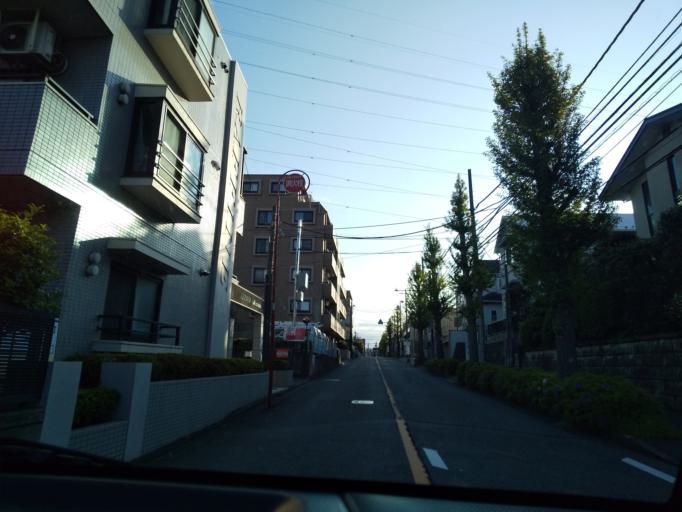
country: JP
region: Tokyo
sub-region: Machida-shi
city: Machida
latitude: 35.5496
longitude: 139.4499
